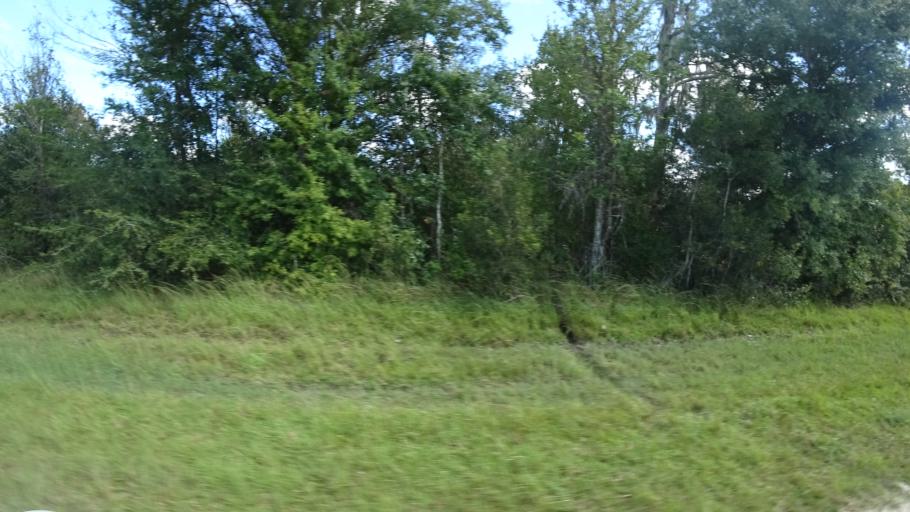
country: US
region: Florida
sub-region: DeSoto County
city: Arcadia
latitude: 27.3580
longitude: -82.1300
